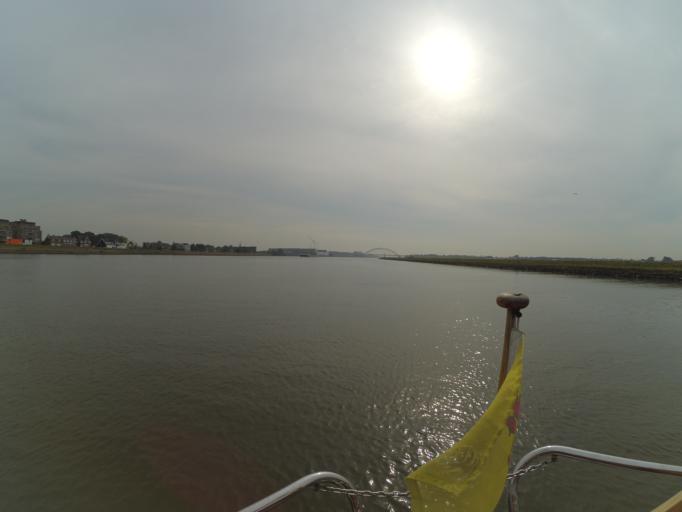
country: NL
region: South Holland
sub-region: Gemeente Alblasserdam
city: Alblasserdam
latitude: 51.8664
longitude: 4.6411
